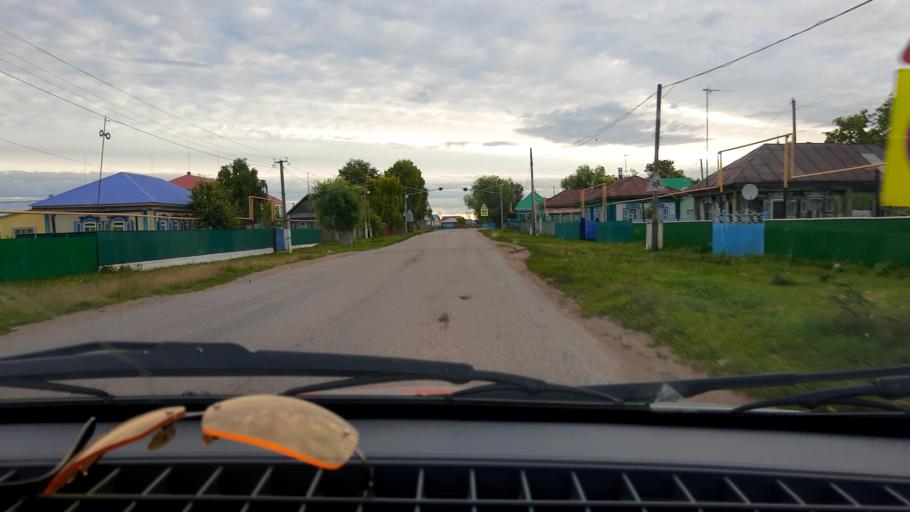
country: RU
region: Bashkortostan
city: Chishmy
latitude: 54.5587
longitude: 55.4667
